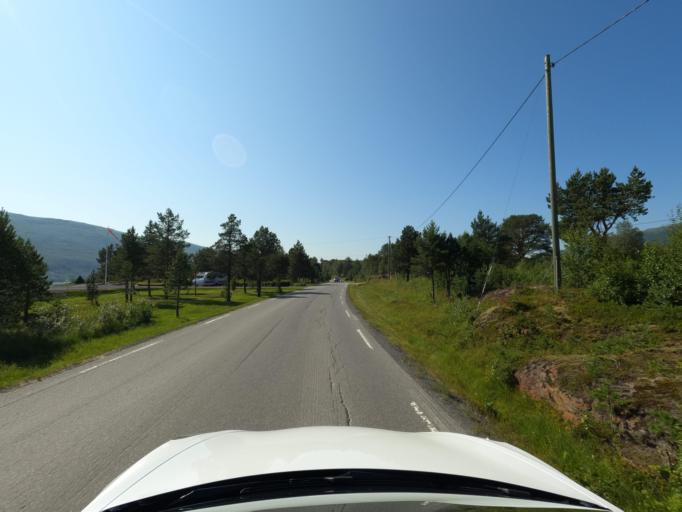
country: NO
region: Nordland
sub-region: Ballangen
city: Ballangen
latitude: 68.3561
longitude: 16.8689
